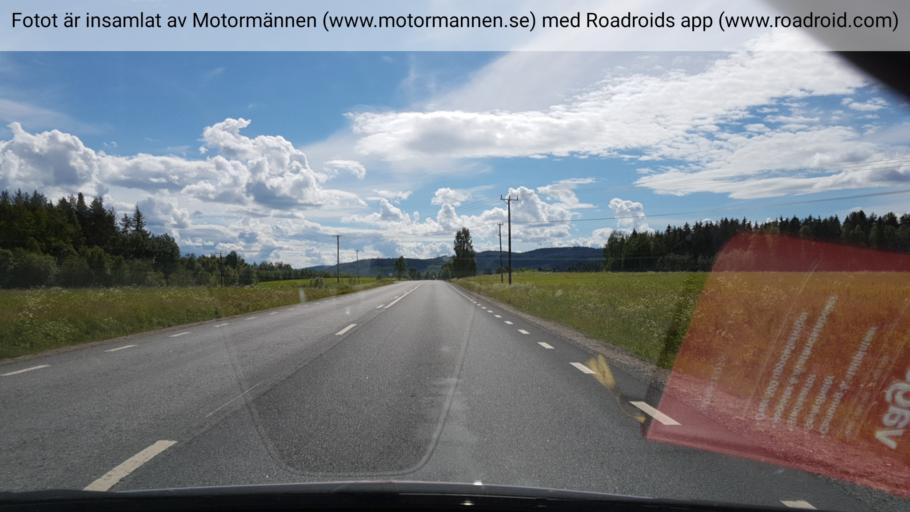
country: SE
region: Vaesternorrland
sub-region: Solleftea Kommun
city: Solleftea
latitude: 63.2512
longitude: 17.2136
